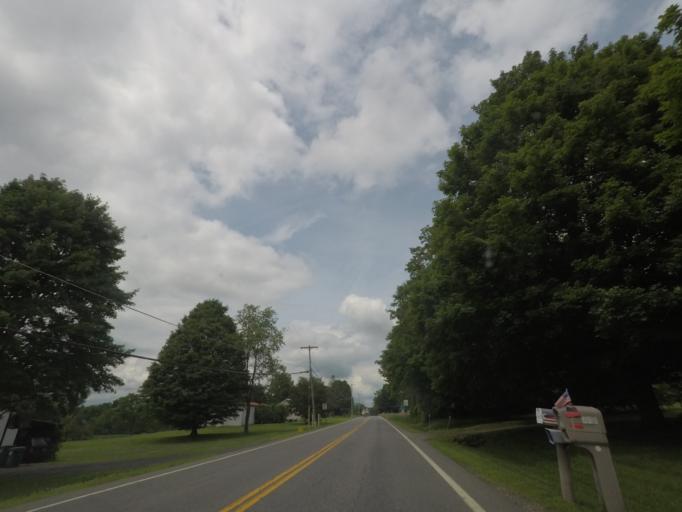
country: US
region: New York
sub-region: Saratoga County
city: Stillwater
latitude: 43.0160
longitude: -73.6924
